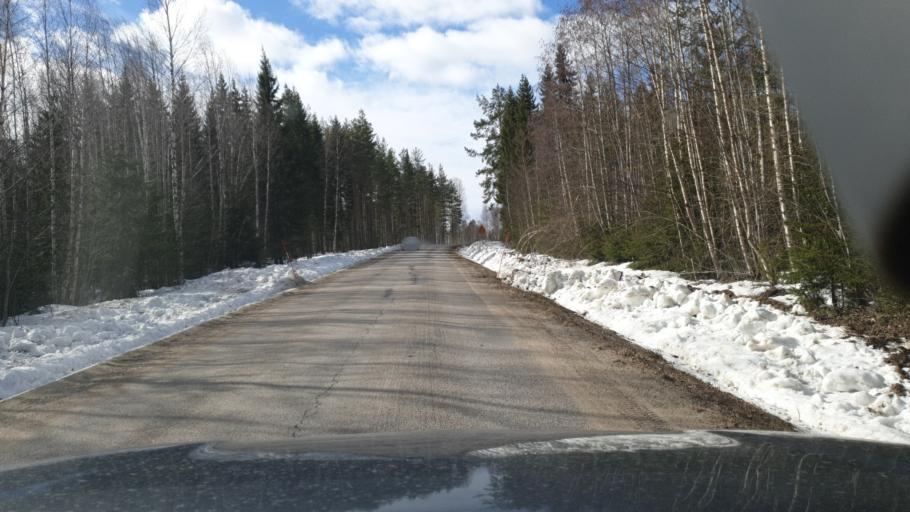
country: SE
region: Gaevleborg
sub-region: Ljusdals Kommun
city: Farila
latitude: 61.8437
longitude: 15.9302
